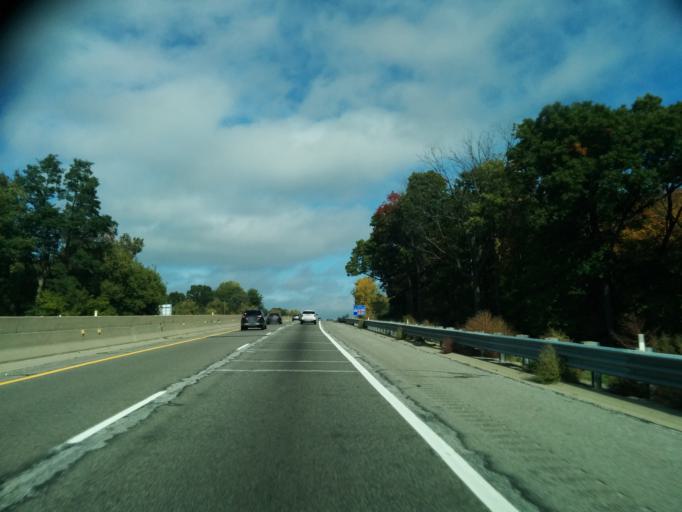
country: US
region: Michigan
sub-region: Livingston County
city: Brighton
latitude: 42.6626
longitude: -83.7593
